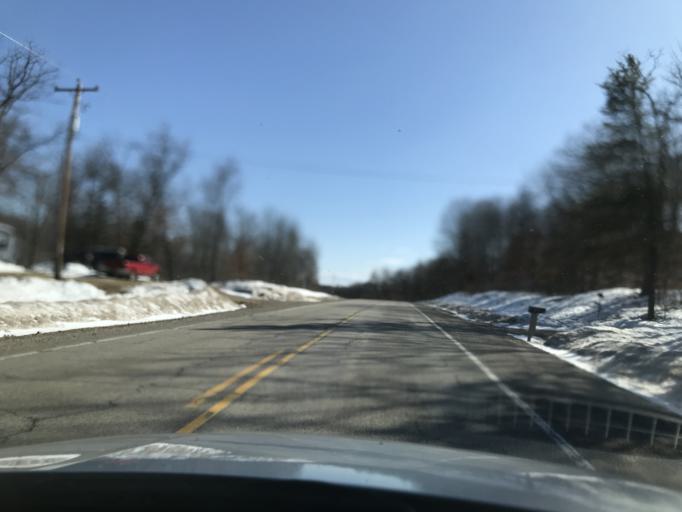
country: US
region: Wisconsin
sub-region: Marinette County
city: Niagara
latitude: 45.3425
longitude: -88.1016
